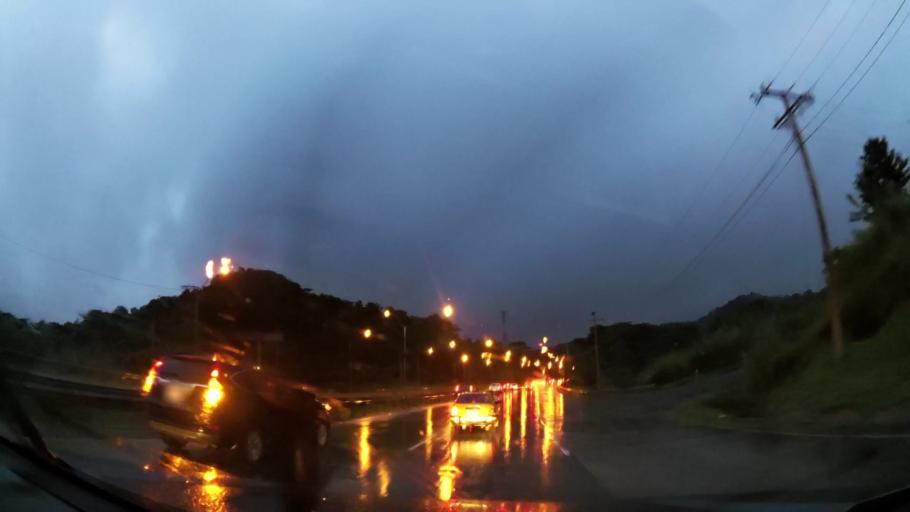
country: PA
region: Panama
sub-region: Distrito de Panama
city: Paraiso
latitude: 9.0221
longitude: -79.6395
